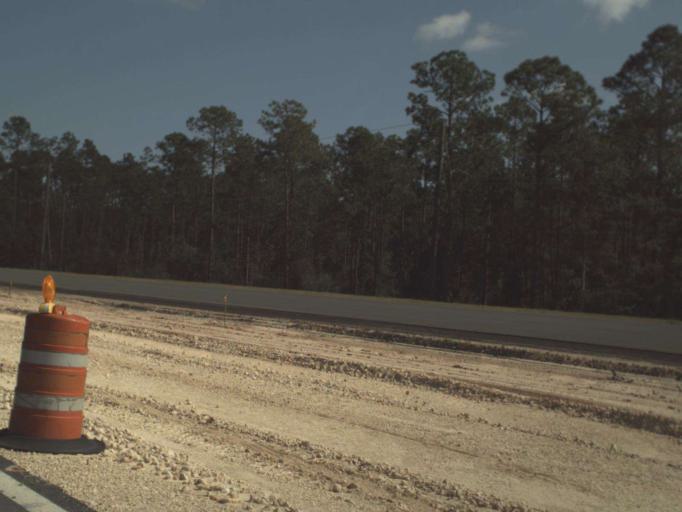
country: US
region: Florida
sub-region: Walton County
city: Freeport
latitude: 30.4506
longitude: -86.1317
